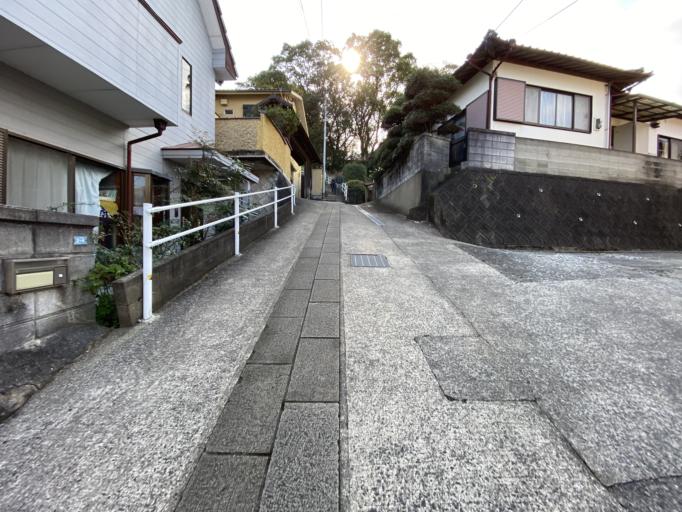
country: JP
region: Nagasaki
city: Nagasaki-shi
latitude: 32.7476
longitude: 129.8866
